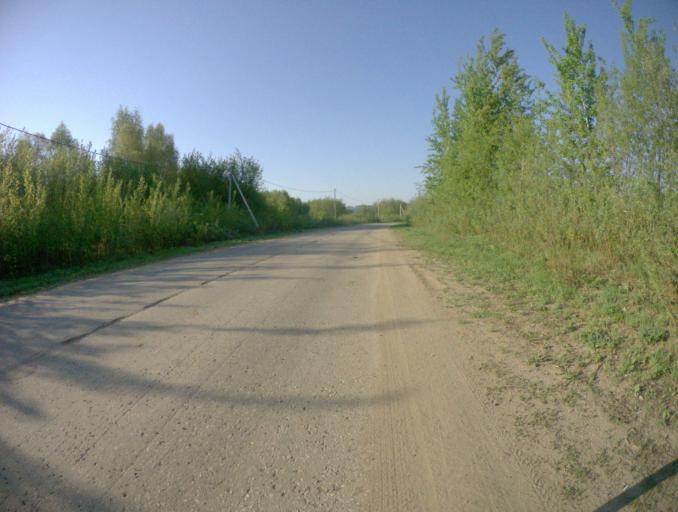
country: RU
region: Vladimir
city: Vyazniki
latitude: 56.2533
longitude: 42.1791
